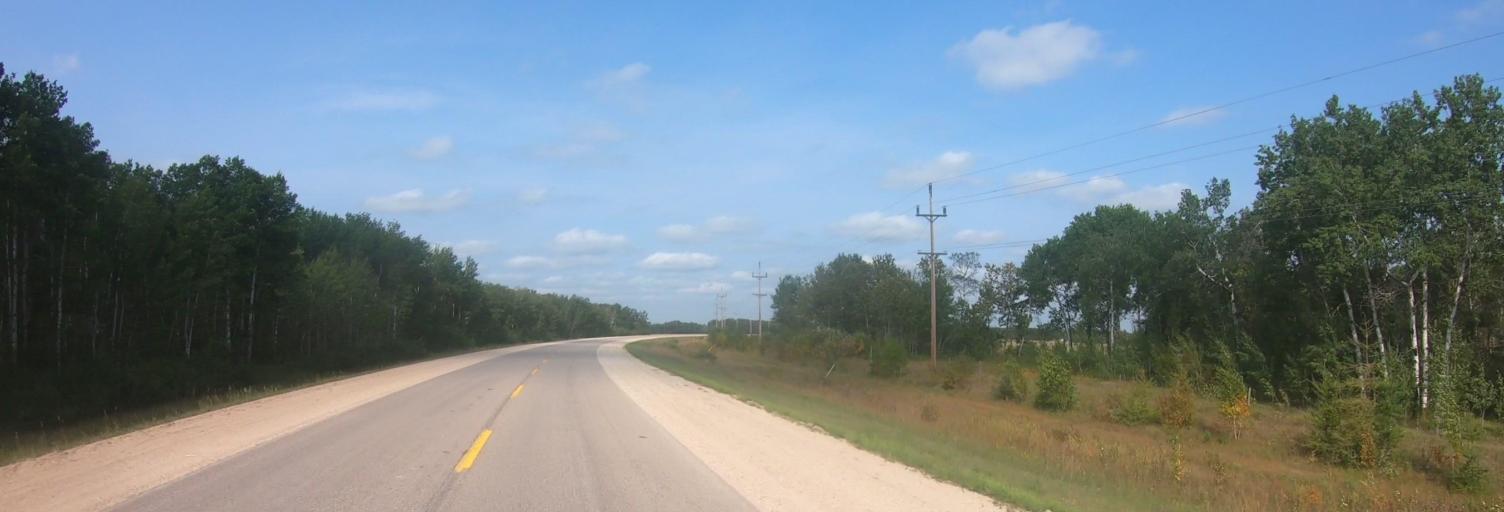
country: CA
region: Manitoba
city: La Broquerie
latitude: 49.1778
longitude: -96.2263
